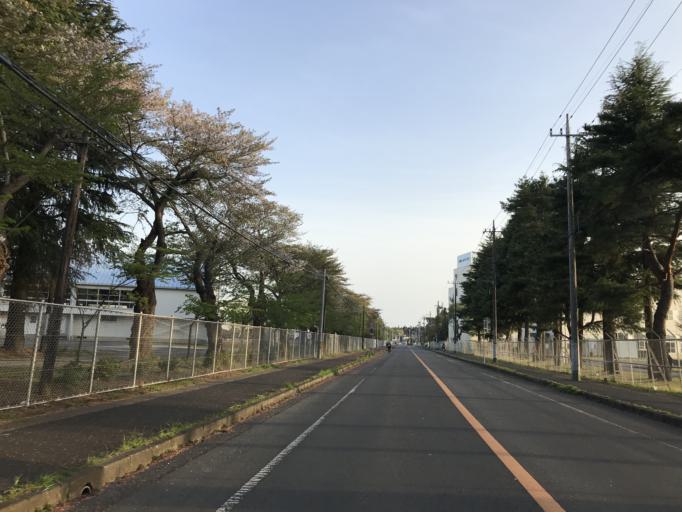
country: JP
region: Ibaraki
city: Katsuta
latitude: 36.3837
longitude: 140.5275
